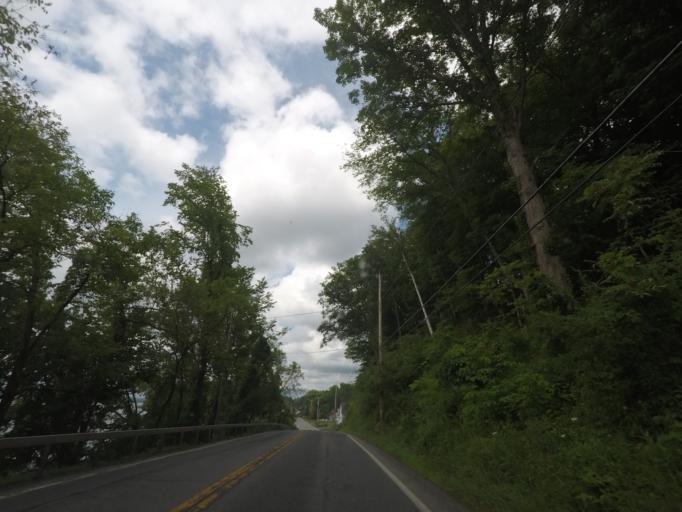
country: US
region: New York
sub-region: Saratoga County
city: Stillwater
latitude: 42.9953
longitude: -73.7358
